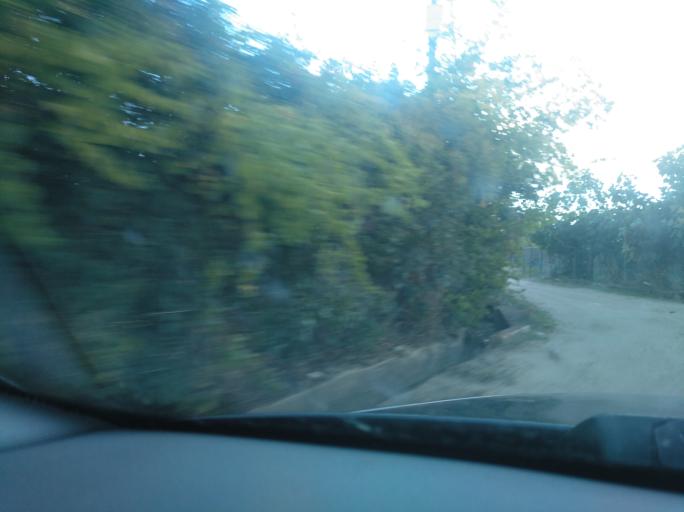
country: PT
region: Portalegre
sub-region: Campo Maior
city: Campo Maior
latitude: 39.0132
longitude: -7.0518
